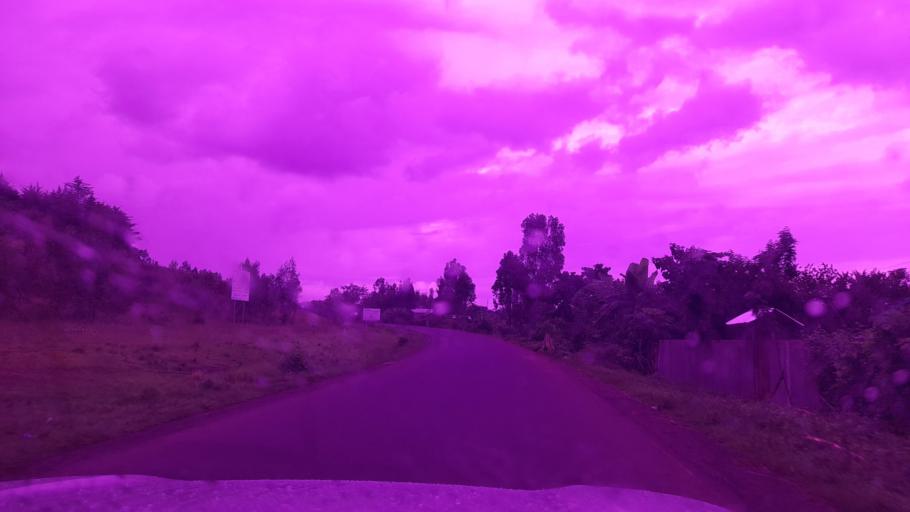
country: ET
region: Oromiya
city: Jima
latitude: 7.7080
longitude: 37.0491
